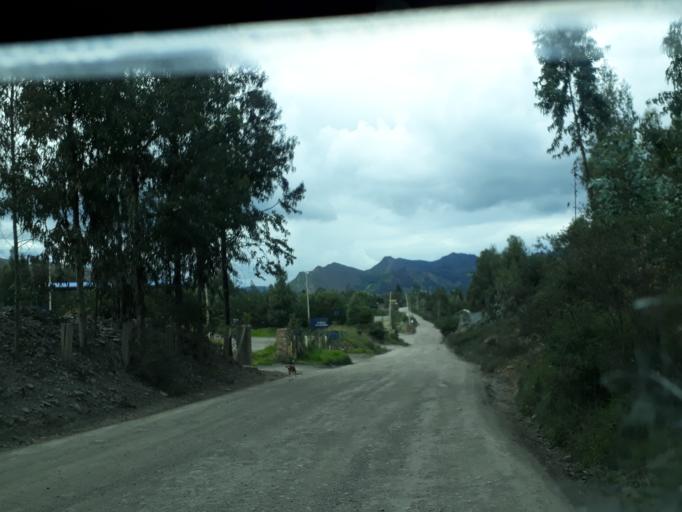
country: CO
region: Cundinamarca
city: Cucunuba
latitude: 5.2395
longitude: -73.7971
